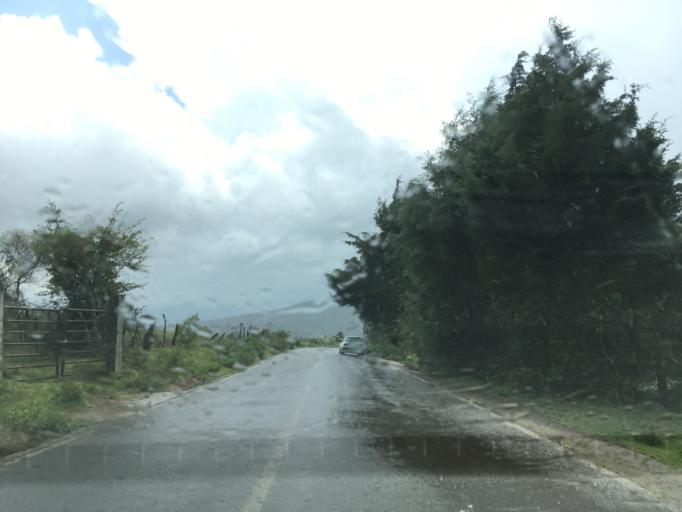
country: MX
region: Michoacan
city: Acuitzio del Canje
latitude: 19.5281
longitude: -101.2350
